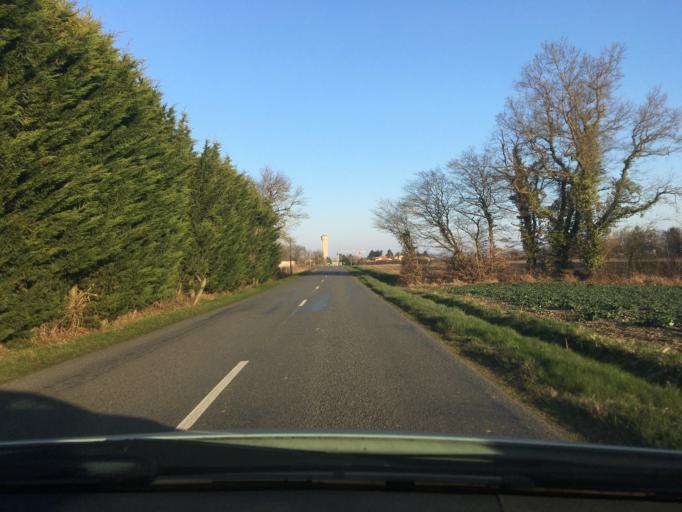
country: FR
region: Rhone-Alpes
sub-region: Departement de l'Ain
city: Amberieux-en-Dombes
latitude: 45.9870
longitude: 4.9154
